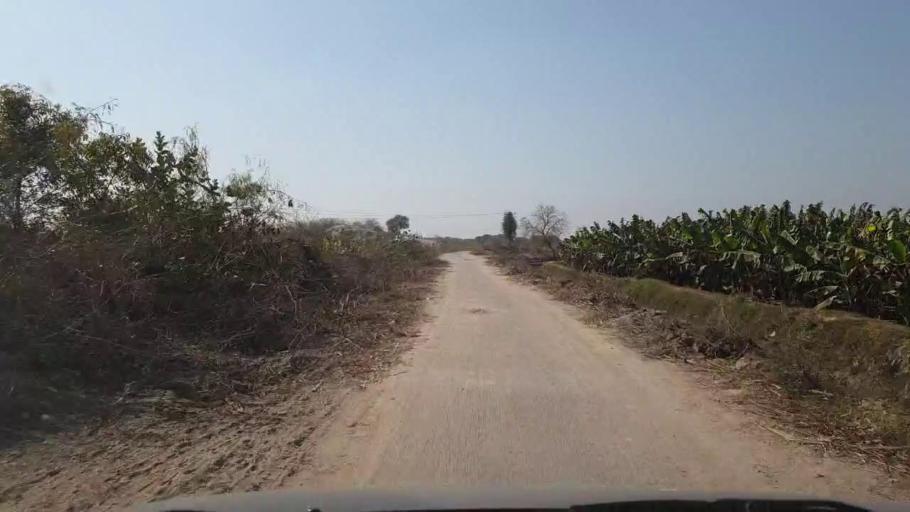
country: PK
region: Sindh
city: Tando Allahyar
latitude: 25.4267
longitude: 68.6339
